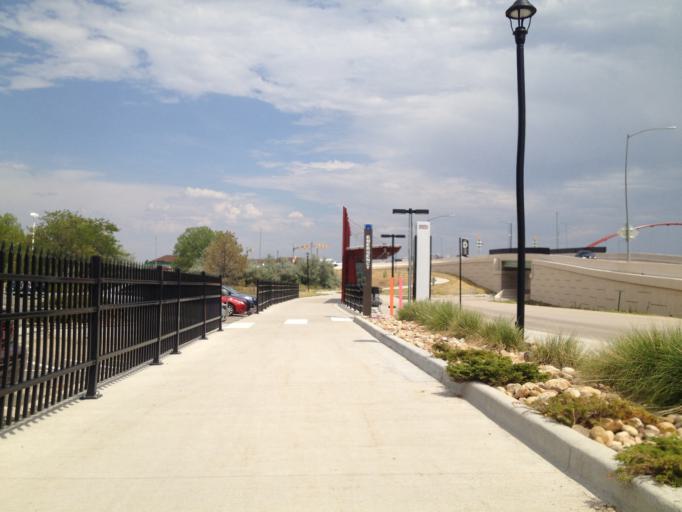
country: US
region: Colorado
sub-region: Boulder County
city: Superior
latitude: 39.9591
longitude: -105.1676
